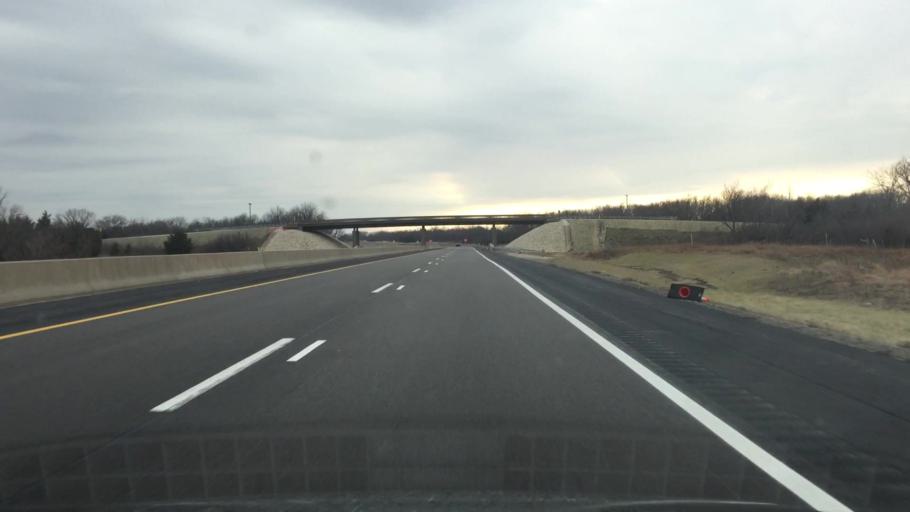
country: US
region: Kansas
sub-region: Osage County
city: Osage City
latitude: 38.7103
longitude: -95.9812
